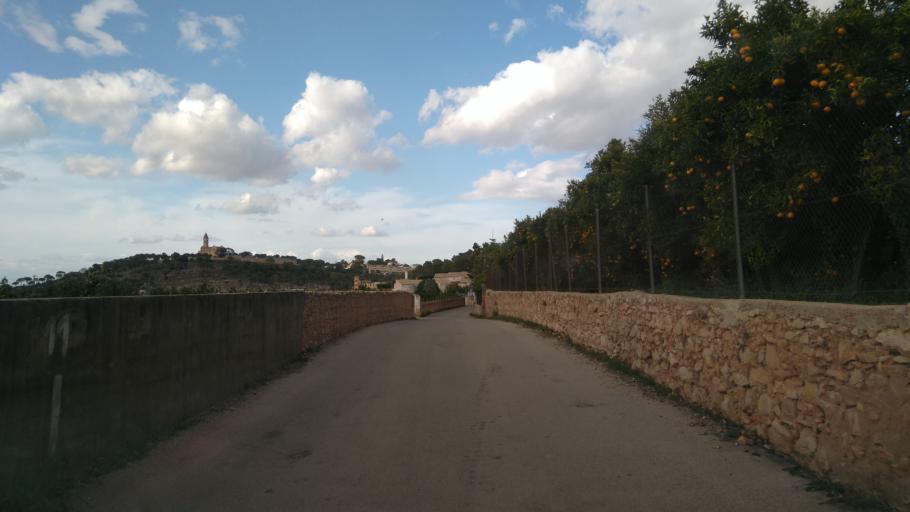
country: ES
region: Valencia
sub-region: Provincia de Valencia
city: Alzira
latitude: 39.1442
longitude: -0.4149
